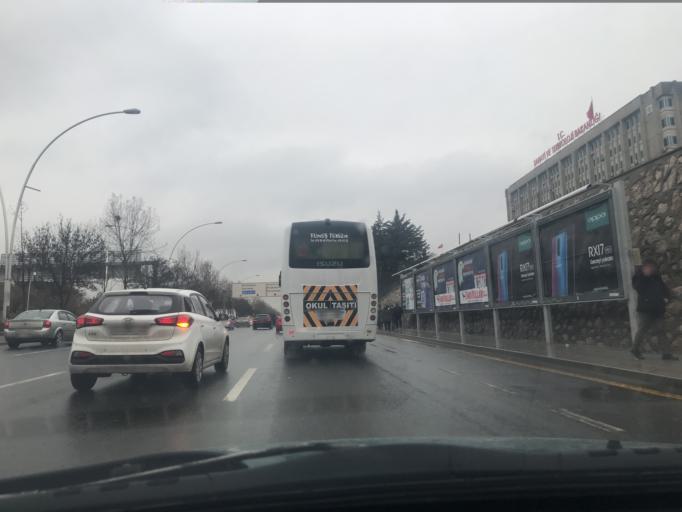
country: TR
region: Ankara
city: Ankara
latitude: 39.9087
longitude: 32.7825
